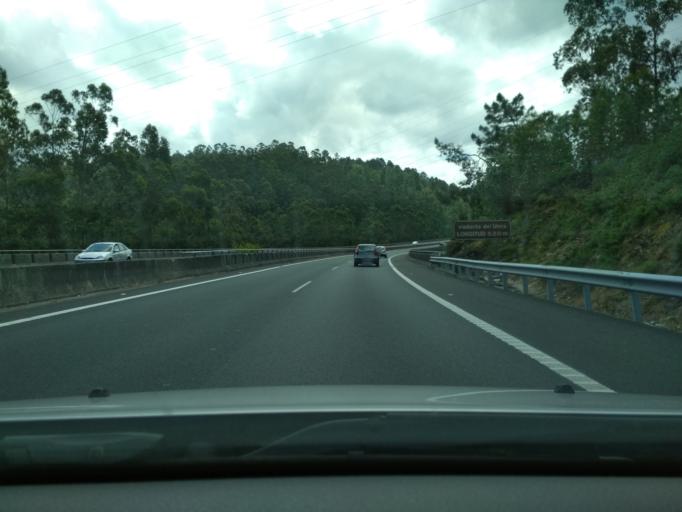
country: ES
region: Galicia
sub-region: Provincia de Pontevedra
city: Portas
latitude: 42.5897
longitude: -8.6762
